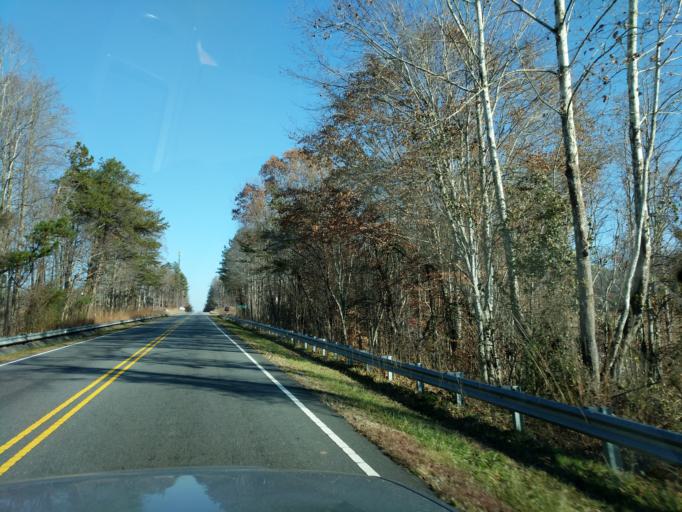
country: US
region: North Carolina
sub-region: Rutherford County
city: Rutherfordton
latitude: 35.4865
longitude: -81.9800
